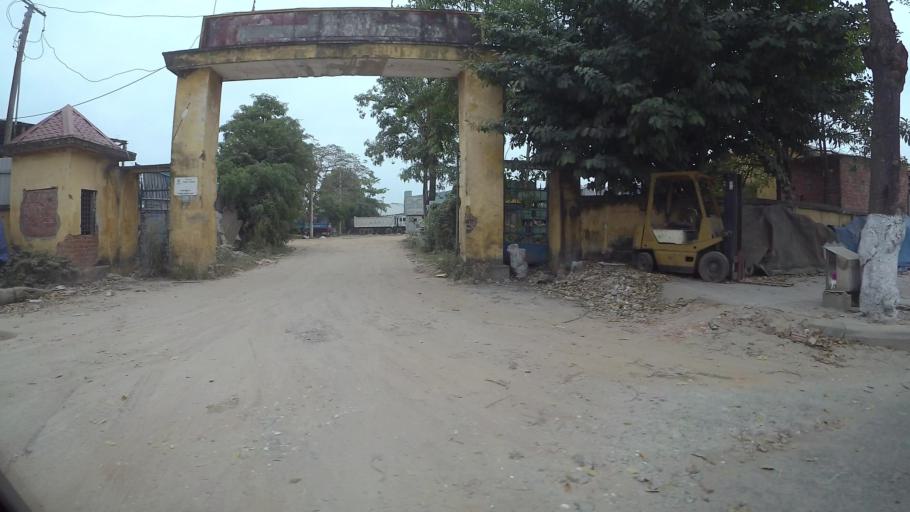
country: VN
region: Da Nang
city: Thanh Khe
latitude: 16.0549
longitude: 108.1812
